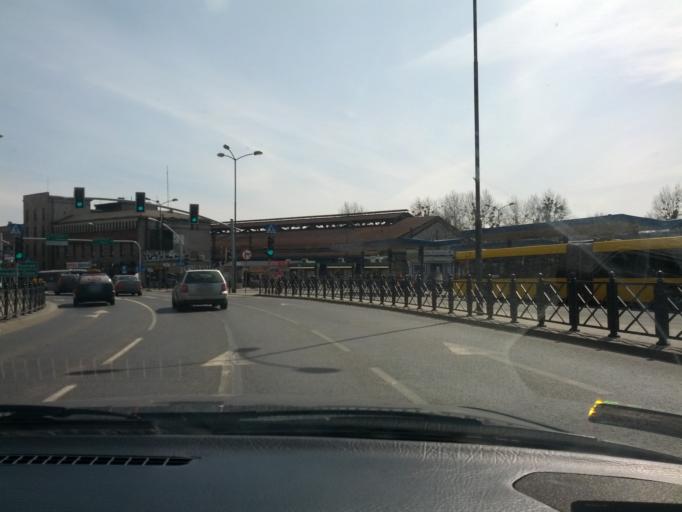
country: PL
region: Silesian Voivodeship
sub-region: Bytom
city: Bytom
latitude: 50.3441
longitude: 18.9133
